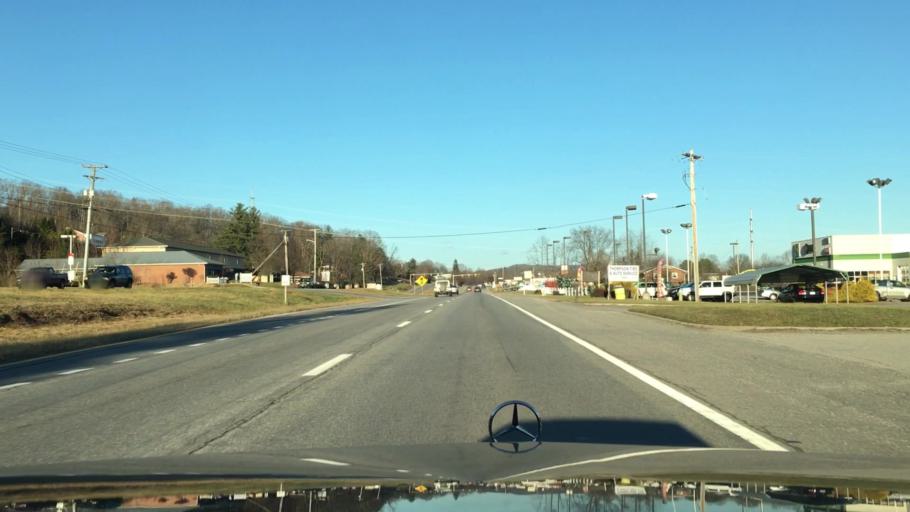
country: US
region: Virginia
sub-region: Montgomery County
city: Merrimac
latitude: 37.1767
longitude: -80.4171
